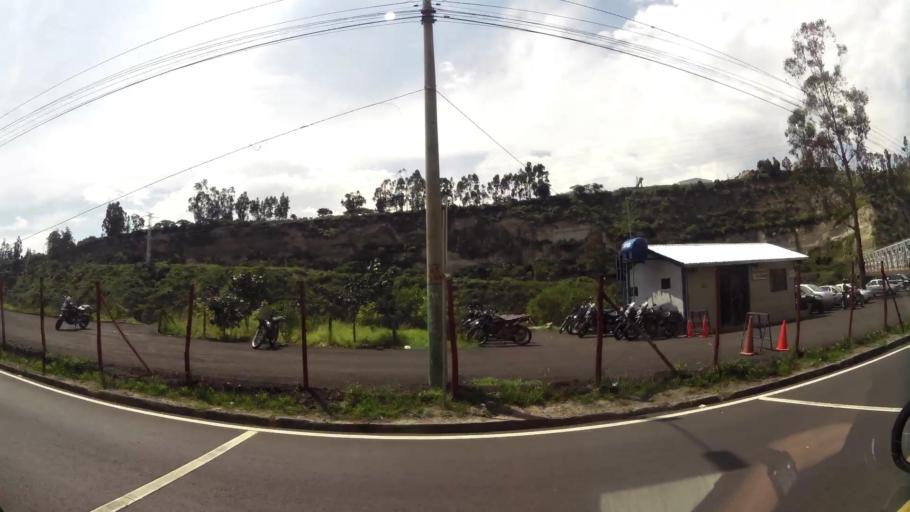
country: EC
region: Pichincha
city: Sangolqui
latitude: -0.2057
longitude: -78.3714
